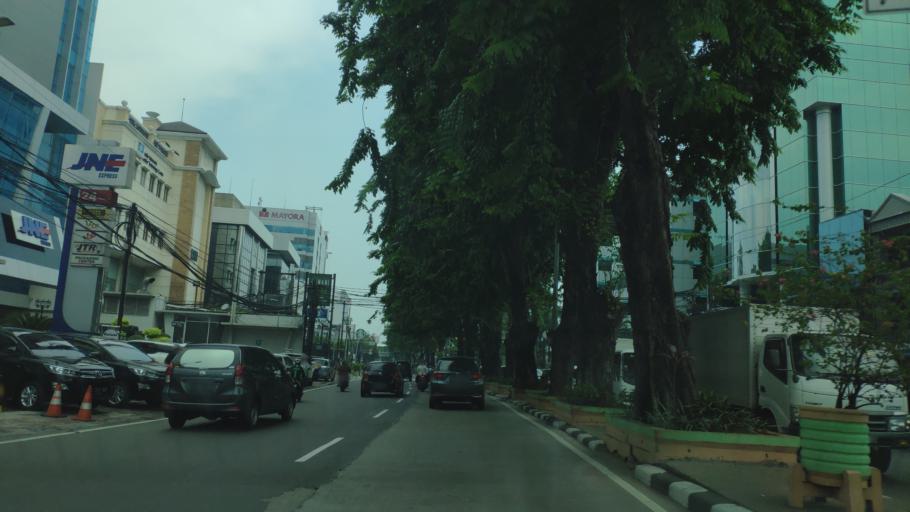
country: ID
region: Jakarta Raya
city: Jakarta
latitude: -6.1785
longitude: 106.7978
